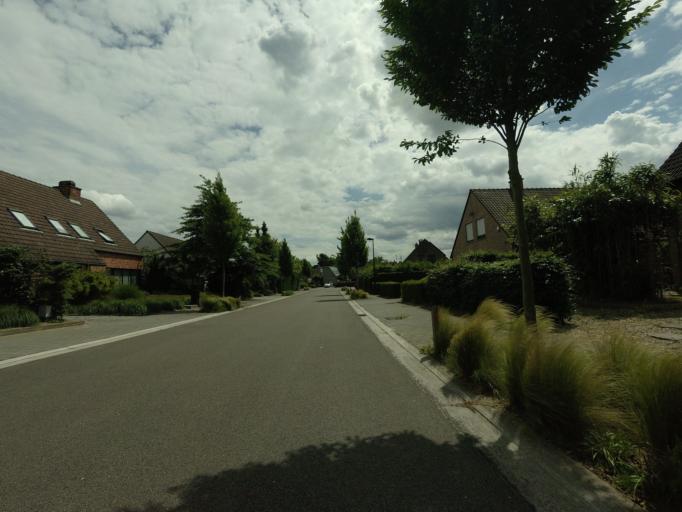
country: BE
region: Flanders
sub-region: Provincie Antwerpen
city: Lint
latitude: 51.1252
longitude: 4.4772
